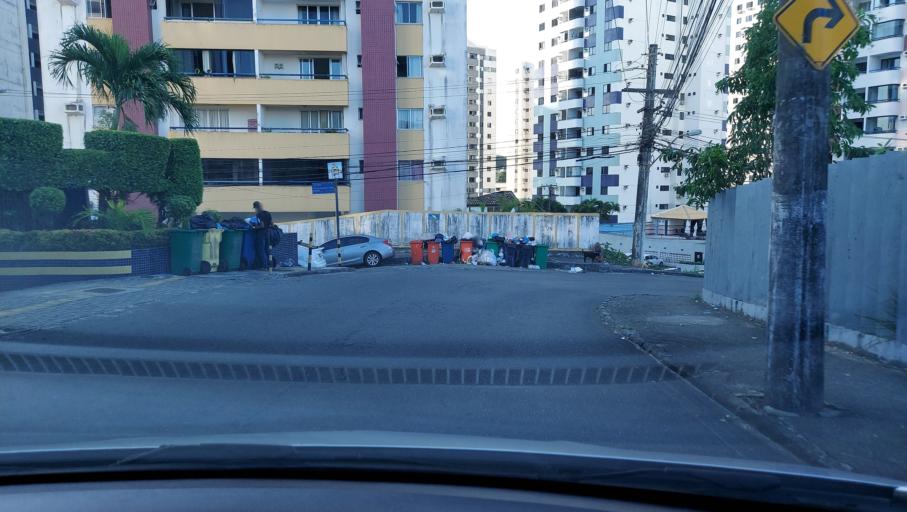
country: BR
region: Bahia
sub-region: Salvador
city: Salvador
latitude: -12.9844
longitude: -38.4426
